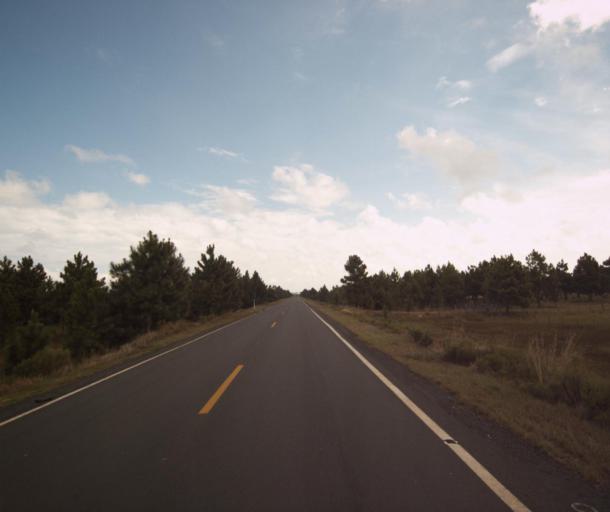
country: BR
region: Rio Grande do Sul
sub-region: Tapes
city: Tapes
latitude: -31.4321
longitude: -51.1904
